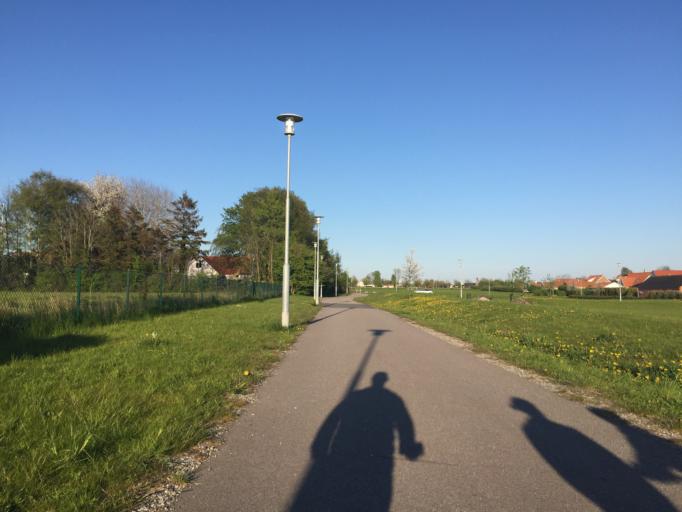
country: SE
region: Skane
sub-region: Malmo
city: Bunkeflostrand
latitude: 55.5534
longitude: 12.9609
